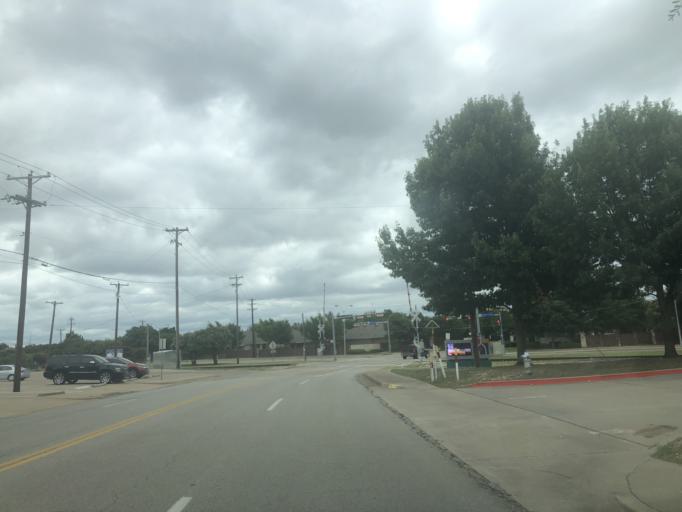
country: US
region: Texas
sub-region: Dallas County
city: Duncanville
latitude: 32.6421
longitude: -96.9202
